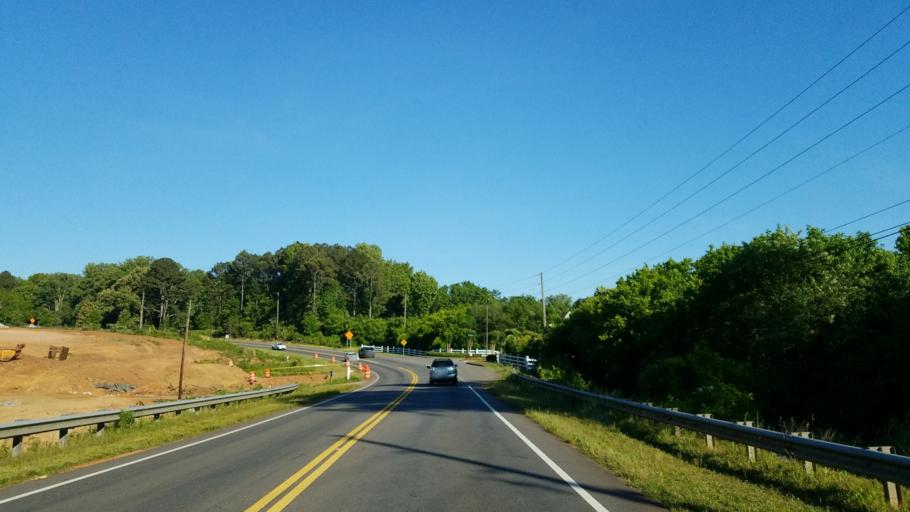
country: US
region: Georgia
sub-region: Cherokee County
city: Holly Springs
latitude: 34.1665
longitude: -84.4363
